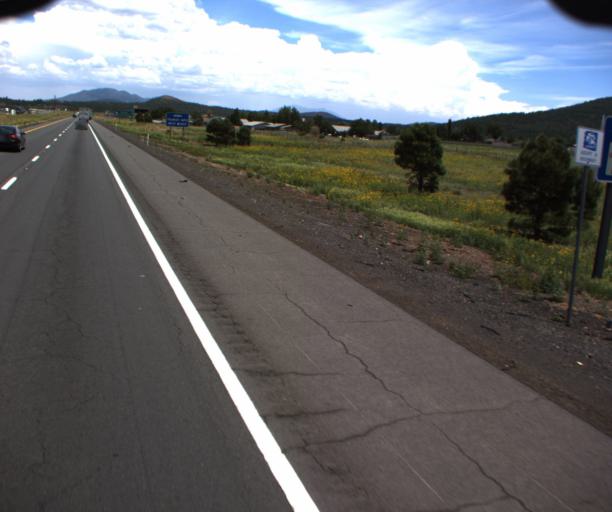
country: US
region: Arizona
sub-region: Coconino County
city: Williams
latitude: 35.2549
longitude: -112.2010
